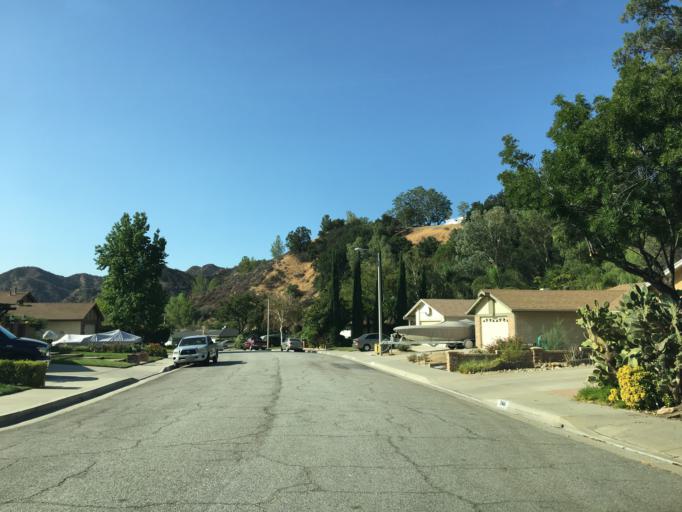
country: US
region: California
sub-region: Los Angeles County
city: Castaic
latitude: 34.4940
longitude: -118.6296
